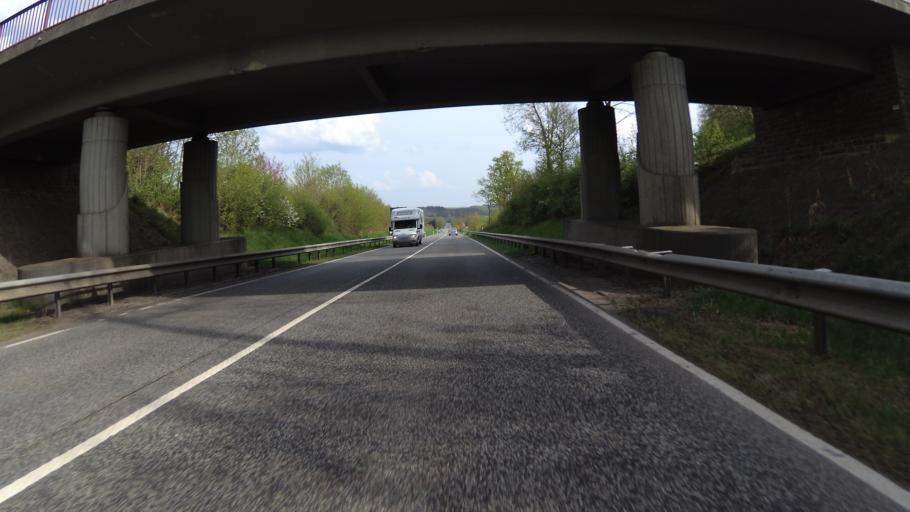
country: DE
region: Rheinland-Pfalz
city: Ulmen
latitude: 50.2050
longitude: 6.9763
